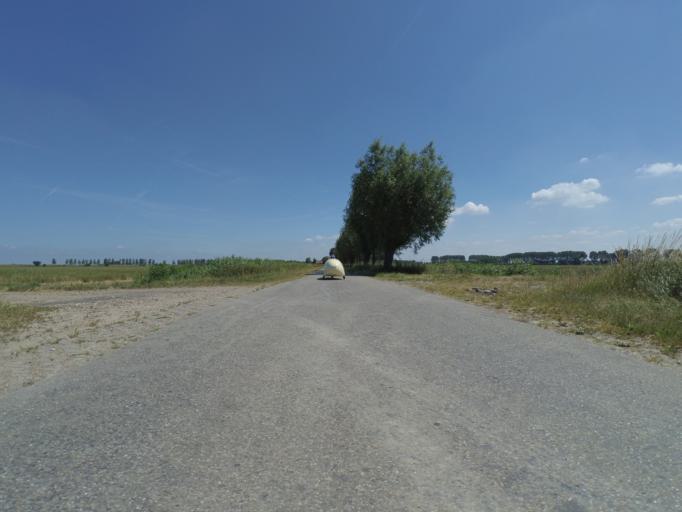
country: NL
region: North Brabant
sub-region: Gemeente Steenbergen
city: Nieuw-Vossemeer
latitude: 51.5930
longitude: 4.1512
